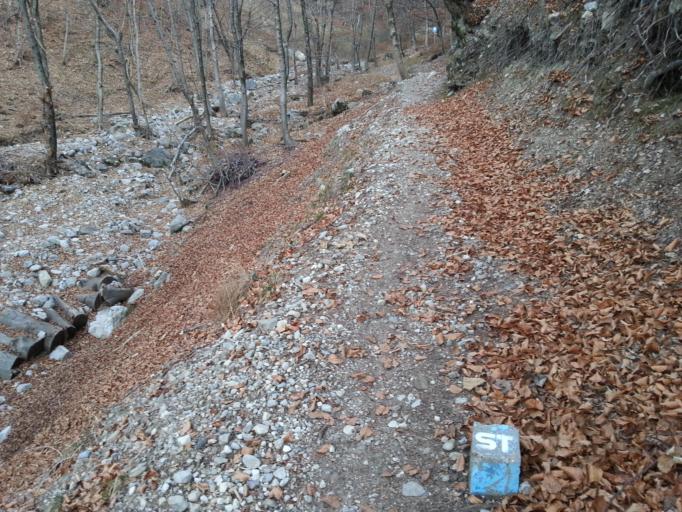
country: CH
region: Ticino
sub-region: Lugano District
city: Pregassona
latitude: 46.0190
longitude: 9.0001
